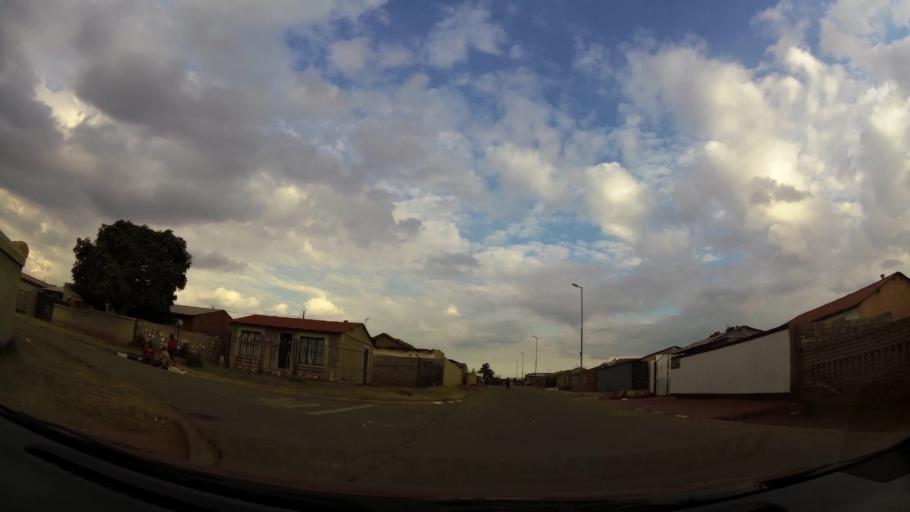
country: ZA
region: Gauteng
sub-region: City of Johannesburg Metropolitan Municipality
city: Soweto
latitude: -26.2416
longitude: 27.8163
